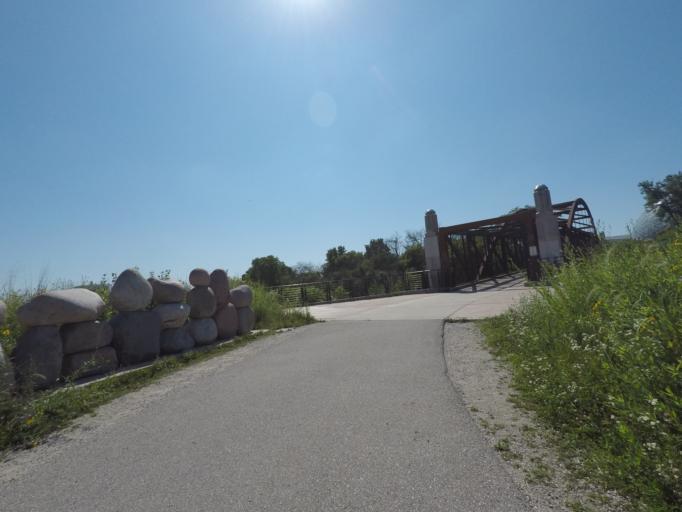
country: US
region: Wisconsin
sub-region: Milwaukee County
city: West Milwaukee
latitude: 43.0282
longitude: -87.9467
